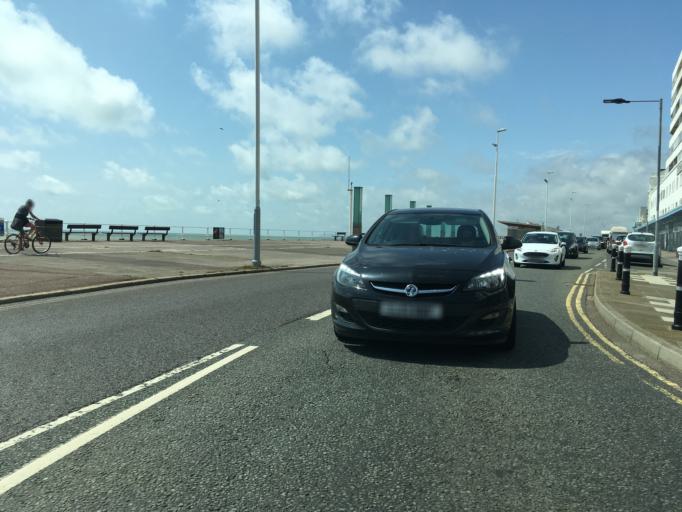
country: GB
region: England
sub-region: East Sussex
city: Saint Leonards-on-Sea
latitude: 50.8510
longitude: 0.5577
